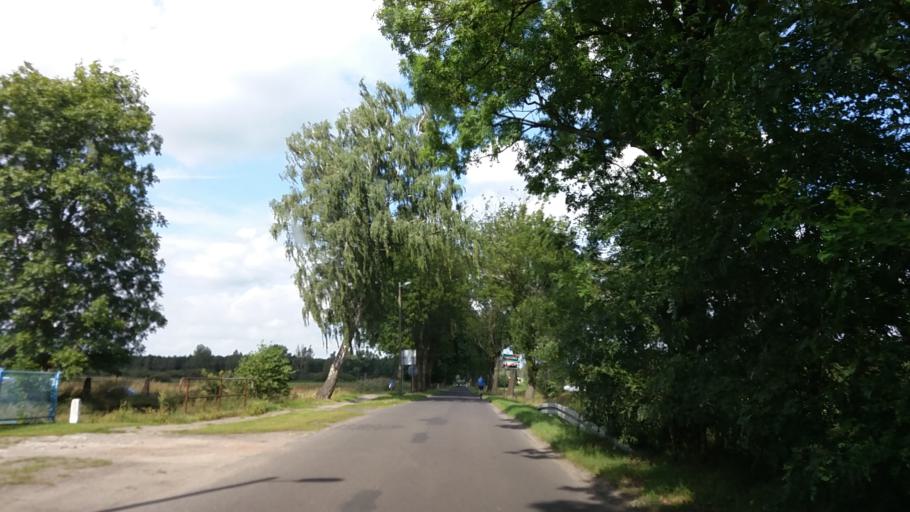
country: PL
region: West Pomeranian Voivodeship
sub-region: Powiat stargardzki
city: Kobylanka
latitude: 53.3683
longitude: 14.8609
